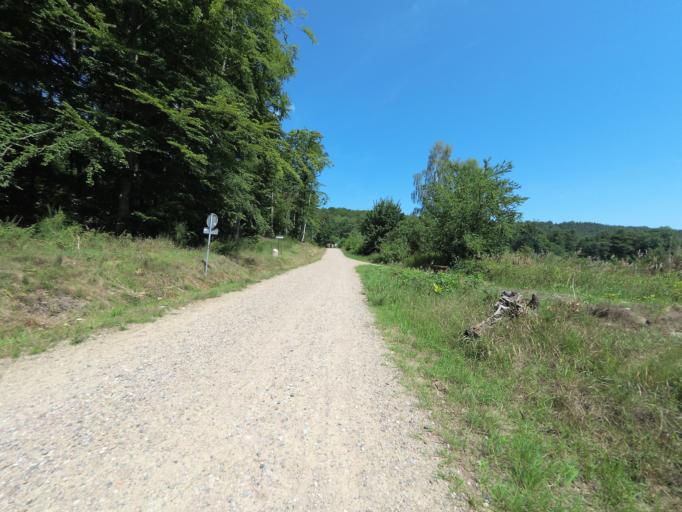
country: PL
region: Pomeranian Voivodeship
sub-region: Gdynia
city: Wielki Kack
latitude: 54.4855
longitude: 18.5008
